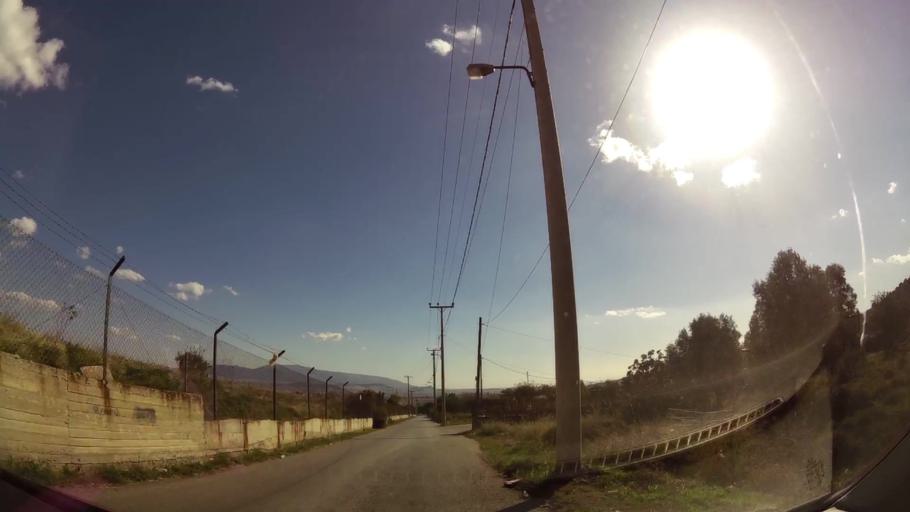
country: GR
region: Attica
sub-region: Nomarchia Anatolikis Attikis
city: Acharnes
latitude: 38.1095
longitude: 23.7225
